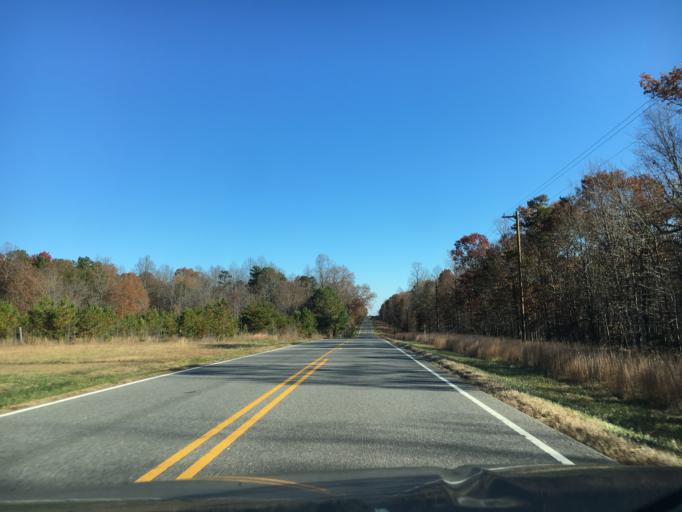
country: US
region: Virginia
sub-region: Buckingham County
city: Buckingham
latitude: 37.4612
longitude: -78.6743
